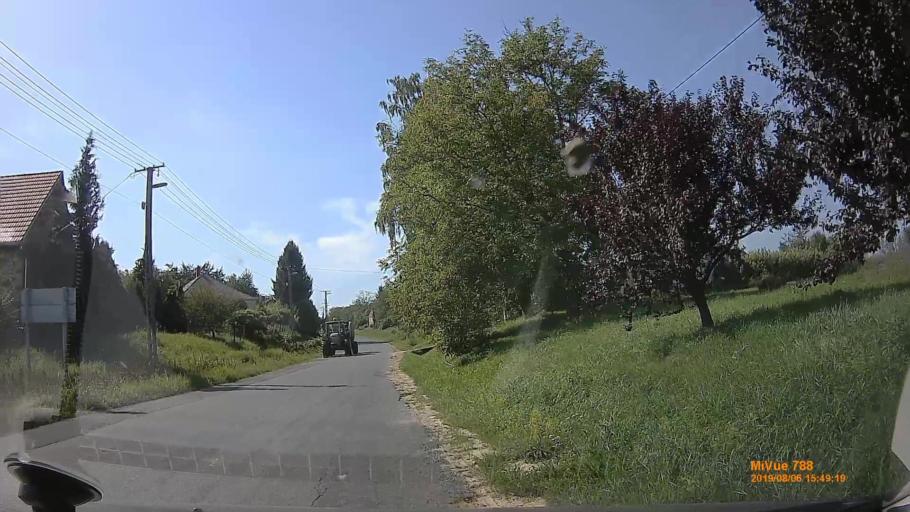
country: HU
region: Somogy
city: Csurgo
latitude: 46.2709
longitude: 17.0448
